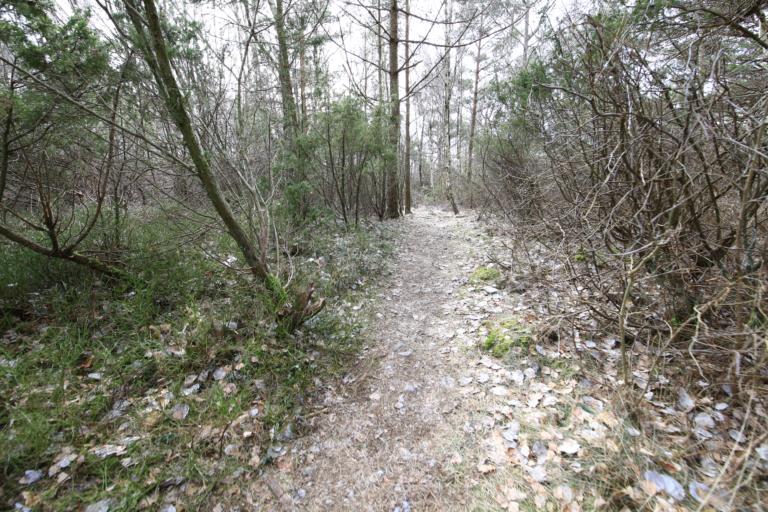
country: SE
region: Halland
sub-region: Kungsbacka Kommun
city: Frillesas
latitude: 57.2320
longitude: 12.1065
